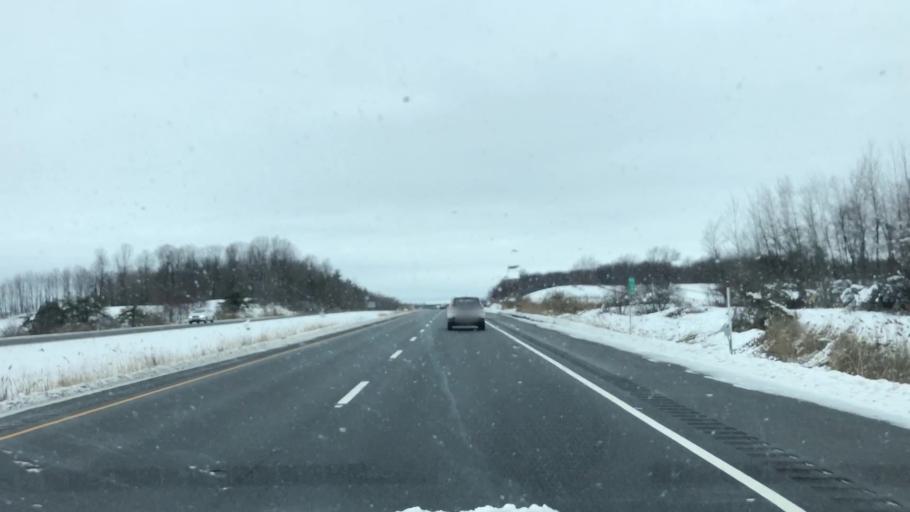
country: CA
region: Quebec
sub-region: Monteregie
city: Granby
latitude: 45.3485
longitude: -72.8134
